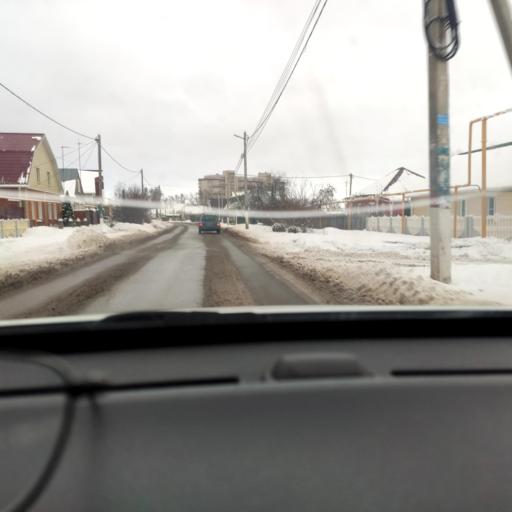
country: RU
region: Voronezj
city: Novaya Usman'
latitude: 51.6483
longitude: 39.4097
